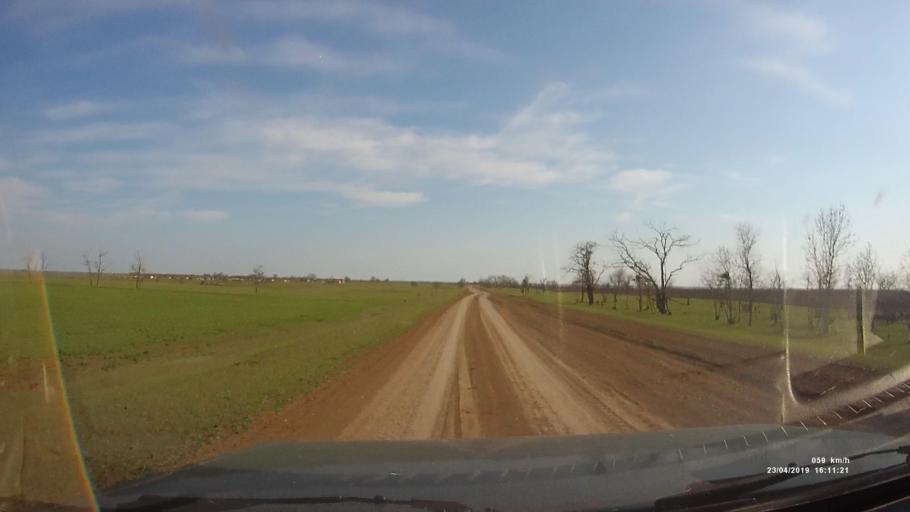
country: RU
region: Rostov
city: Remontnoye
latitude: 46.4746
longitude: 43.1231
